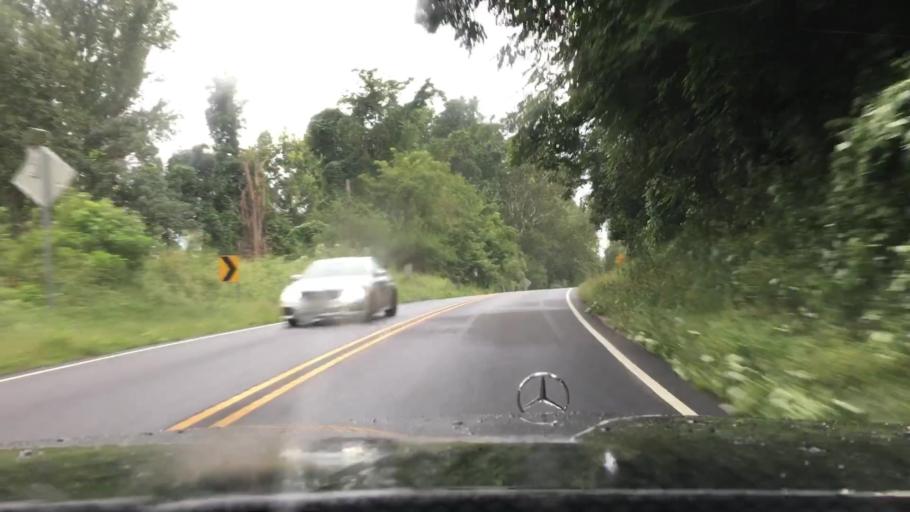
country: US
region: Virginia
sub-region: Nelson County
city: Nellysford
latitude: 37.8845
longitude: -78.9001
